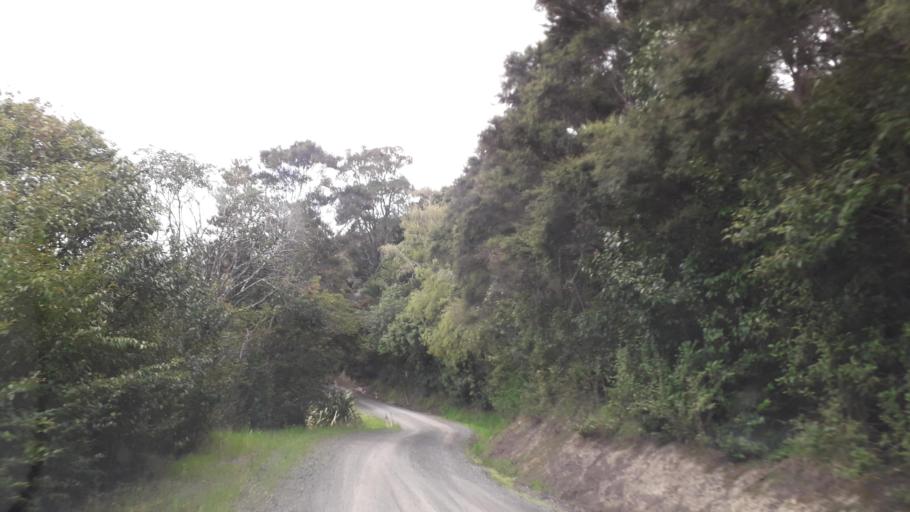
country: NZ
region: Northland
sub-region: Far North District
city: Waimate North
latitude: -35.3087
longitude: 173.5636
